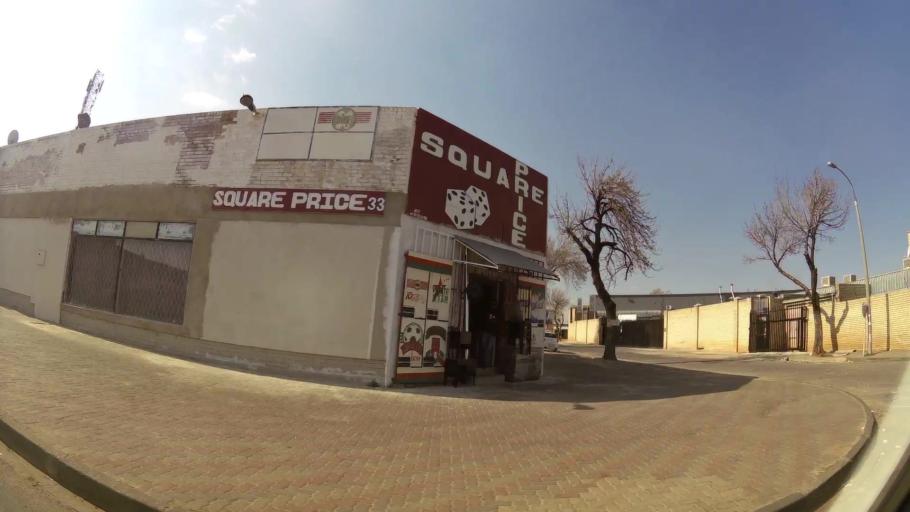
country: ZA
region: Gauteng
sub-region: Ekurhuleni Metropolitan Municipality
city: Germiston
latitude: -26.1905
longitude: 28.2052
